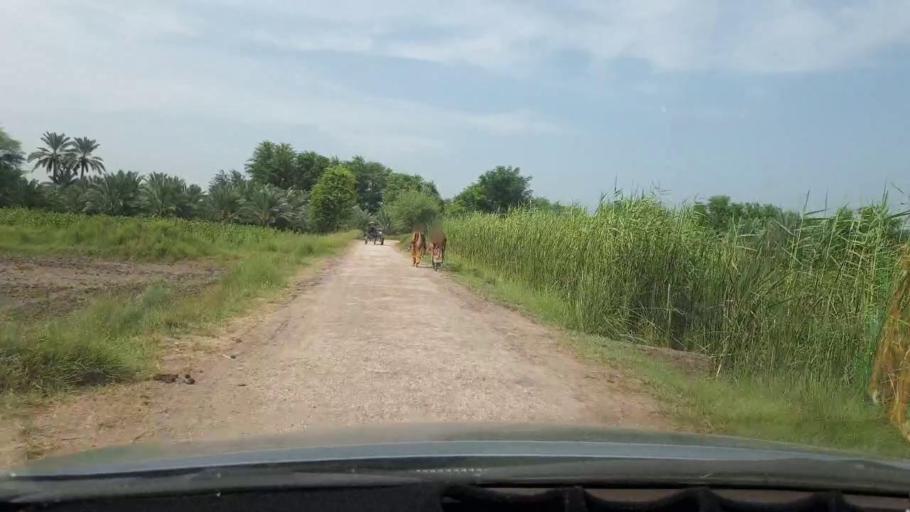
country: PK
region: Sindh
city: Khairpur
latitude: 27.4827
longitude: 68.7476
